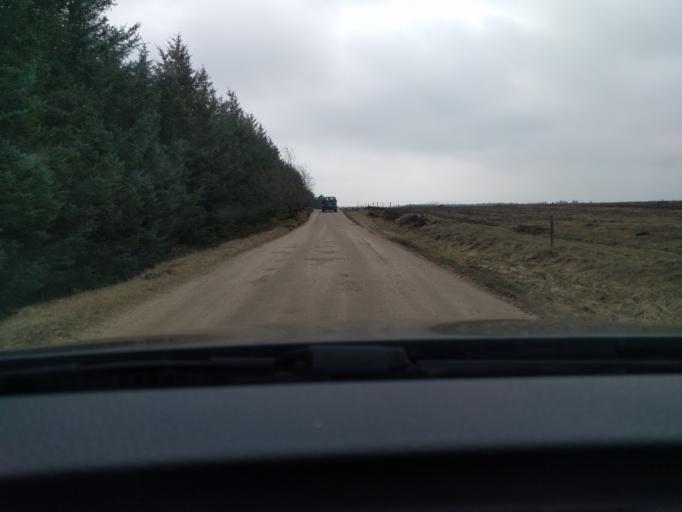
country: DK
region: Central Jutland
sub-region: Skive Kommune
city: Skive
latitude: 56.5058
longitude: 8.9426
